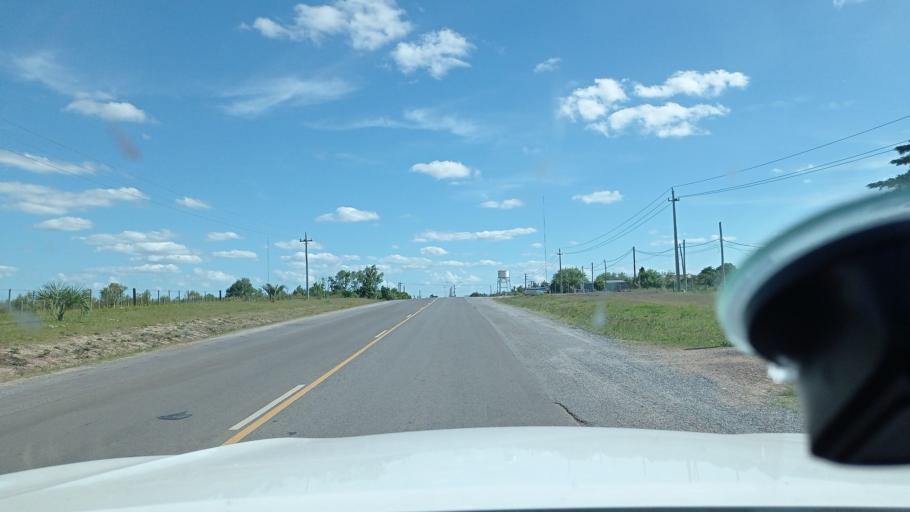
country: UY
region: Florida
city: Florida
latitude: -34.0833
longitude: -56.2364
